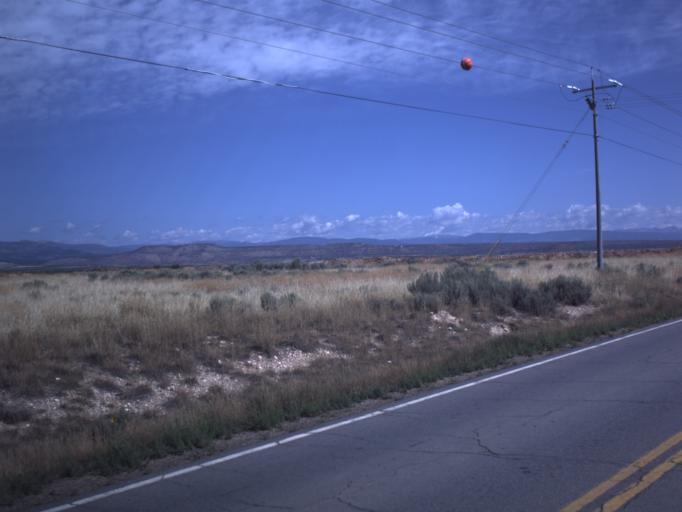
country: US
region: Utah
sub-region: Duchesne County
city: Duchesne
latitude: 40.1947
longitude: -110.3918
